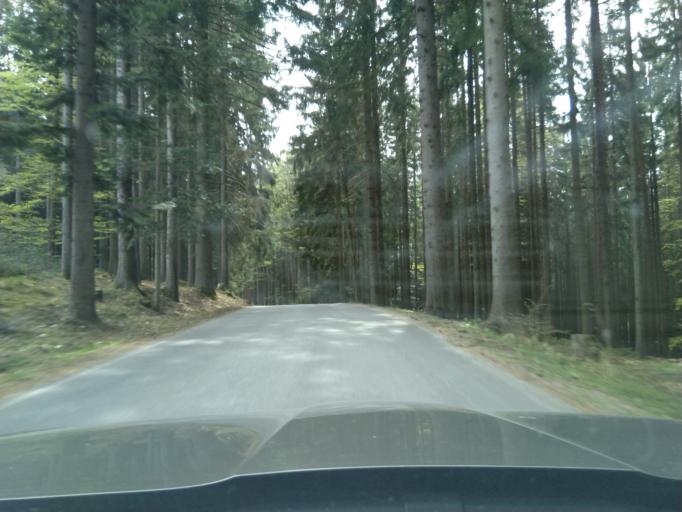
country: CZ
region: Jihocesky
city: Vacov
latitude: 49.1566
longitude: 13.6912
